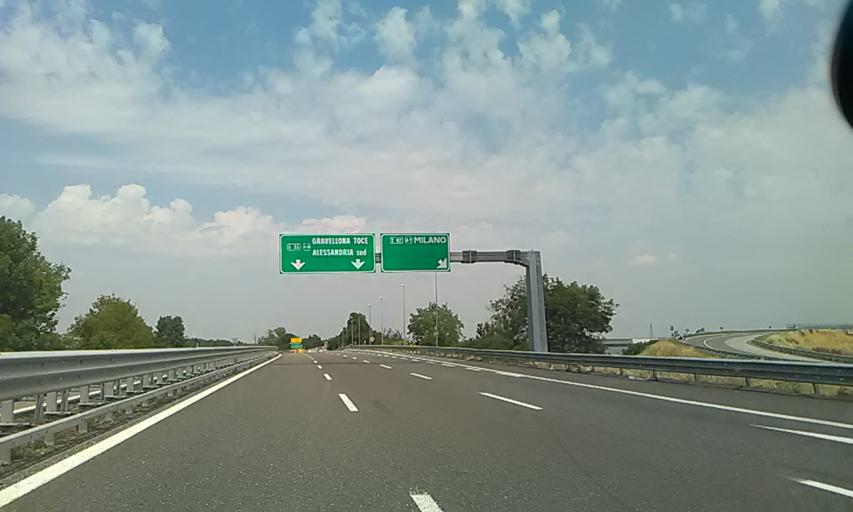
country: IT
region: Piedmont
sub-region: Provincia di Alessandria
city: Predosa
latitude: 44.7552
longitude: 8.6460
